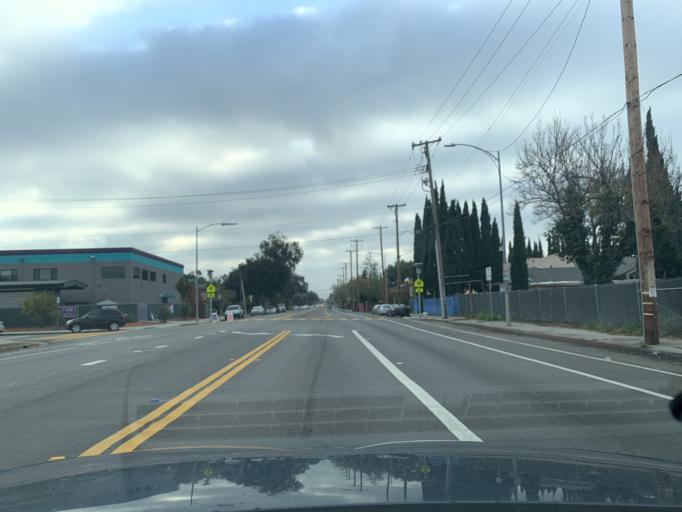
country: US
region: California
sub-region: Santa Clara County
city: San Jose
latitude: 37.3293
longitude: -121.8567
